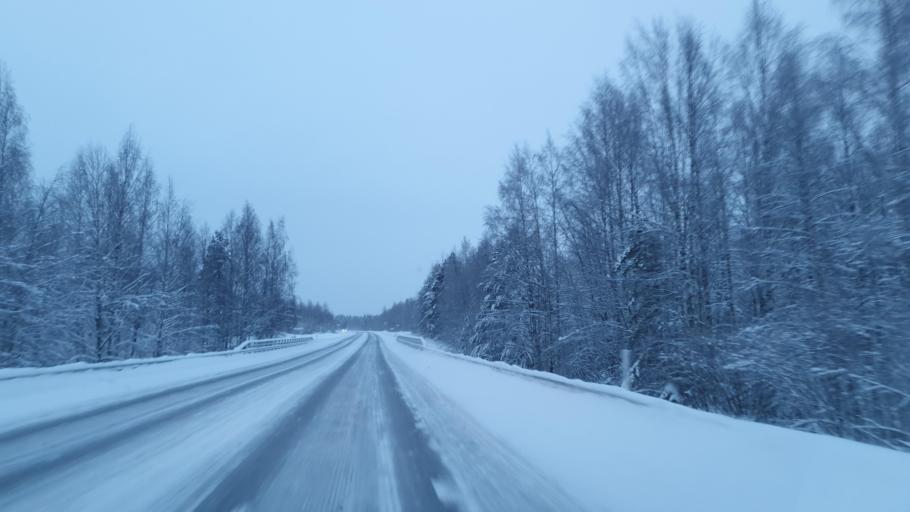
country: FI
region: Kainuu
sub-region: Kajaani
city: Vaala
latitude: 64.5949
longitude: 26.7908
